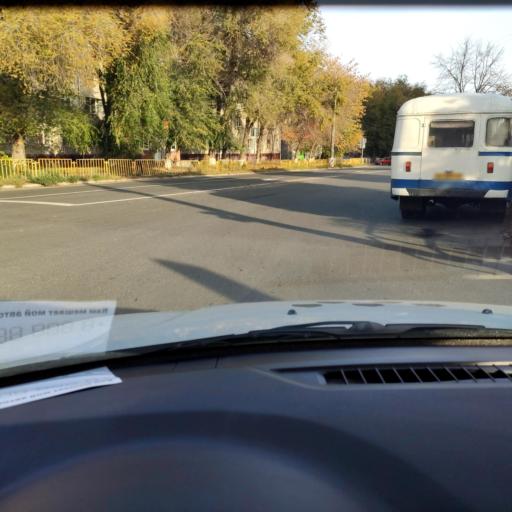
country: RU
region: Samara
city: Tol'yatti
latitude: 53.5211
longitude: 49.4268
